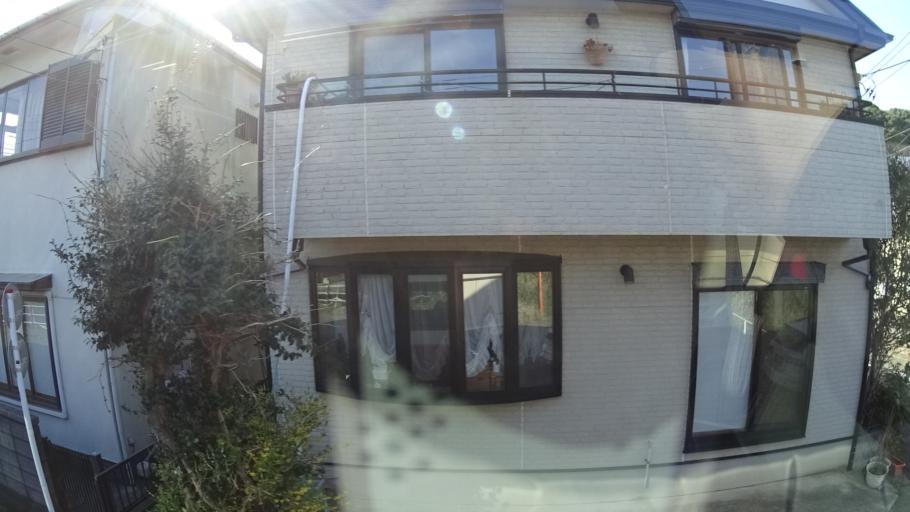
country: JP
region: Kanagawa
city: Miura
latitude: 35.1607
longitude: 139.6412
